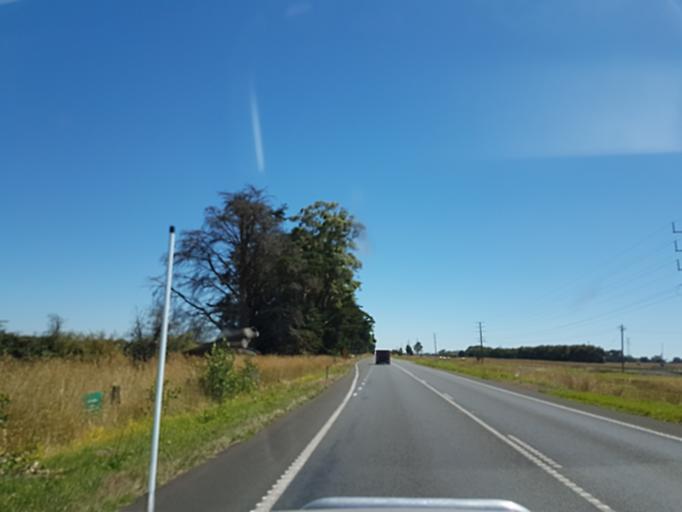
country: AU
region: Victoria
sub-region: Warrnambool
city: Allansford
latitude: -38.2305
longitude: 142.9459
